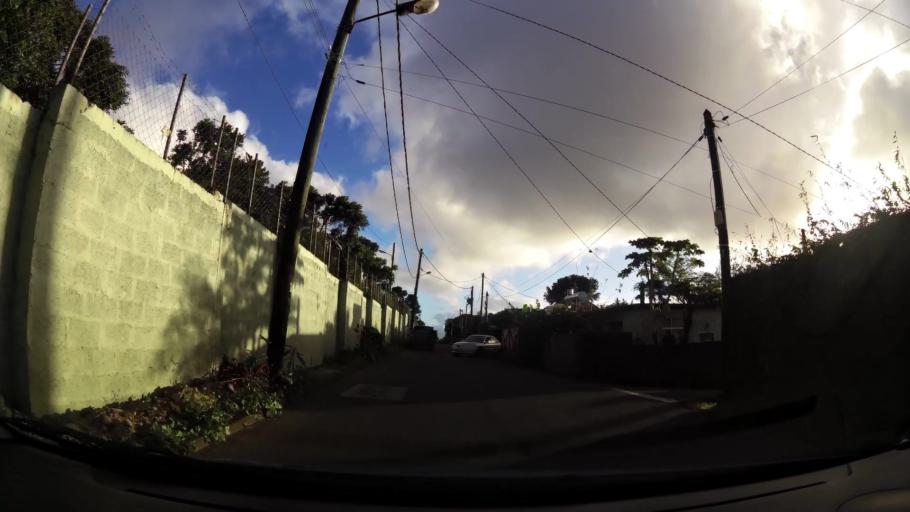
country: MU
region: Plaines Wilhems
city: Curepipe
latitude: -20.3117
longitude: 57.5338
